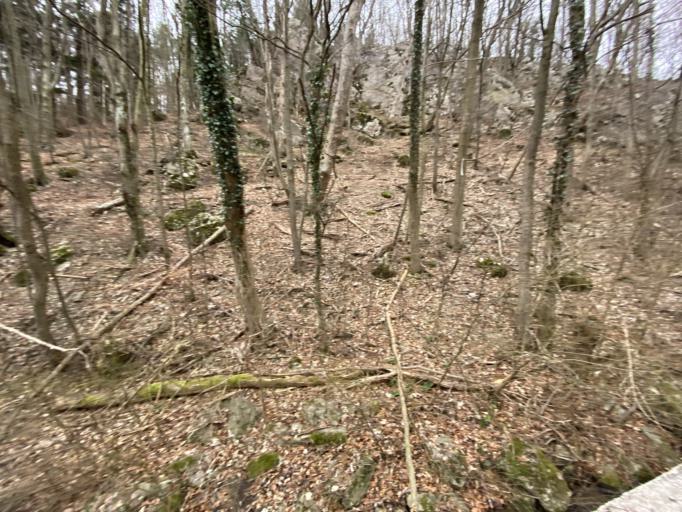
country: AT
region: Lower Austria
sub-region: Politischer Bezirk Modling
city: Gaaden
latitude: 48.0214
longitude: 16.1901
